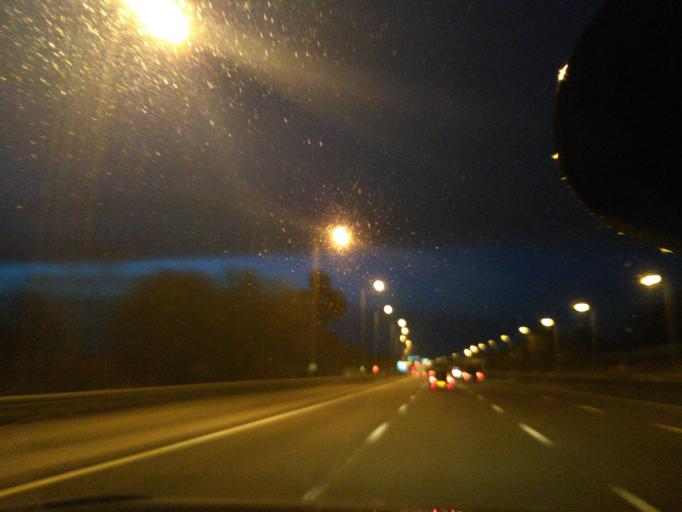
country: GB
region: England
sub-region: Derbyshire
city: Pinxton
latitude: 53.0764
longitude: -1.2889
